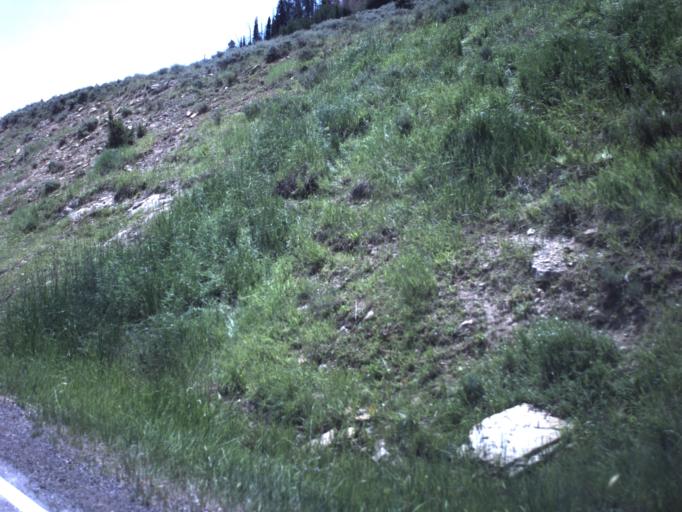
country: US
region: Utah
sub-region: Sanpete County
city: Fairview
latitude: 39.6592
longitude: -111.2422
